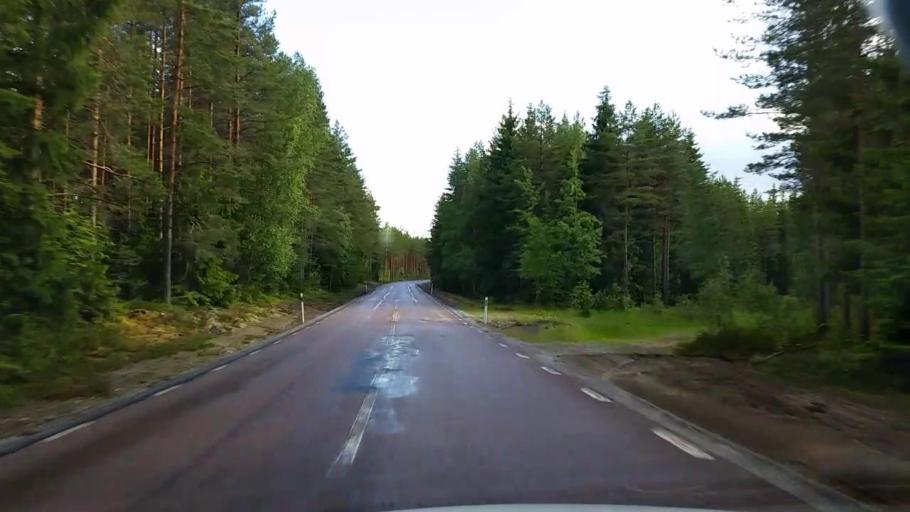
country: SE
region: Vaestmanland
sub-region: Fagersta Kommun
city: Fagersta
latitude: 59.9065
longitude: 15.8229
